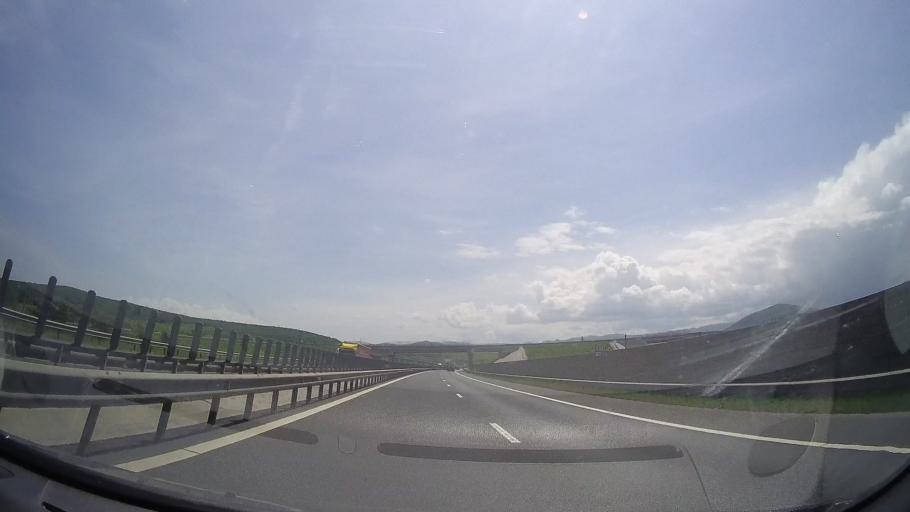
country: RO
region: Sibiu
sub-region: Comuna Orlat
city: Orlat
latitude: 45.7890
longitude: 23.9441
